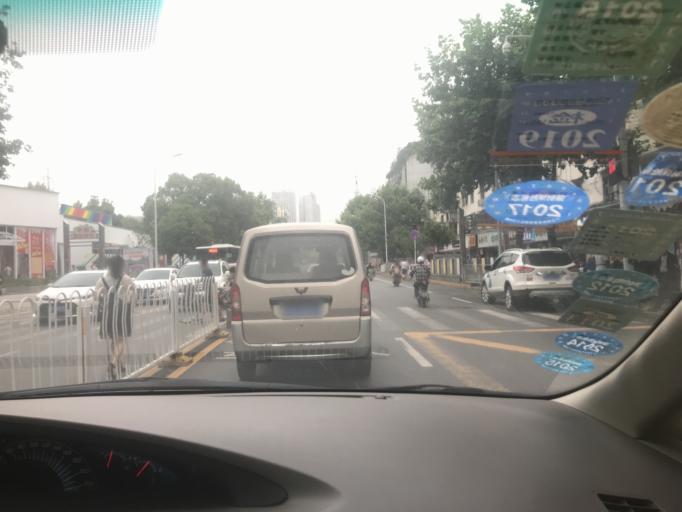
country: CN
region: Hubei
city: Wuhan
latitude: 30.5523
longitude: 114.2626
